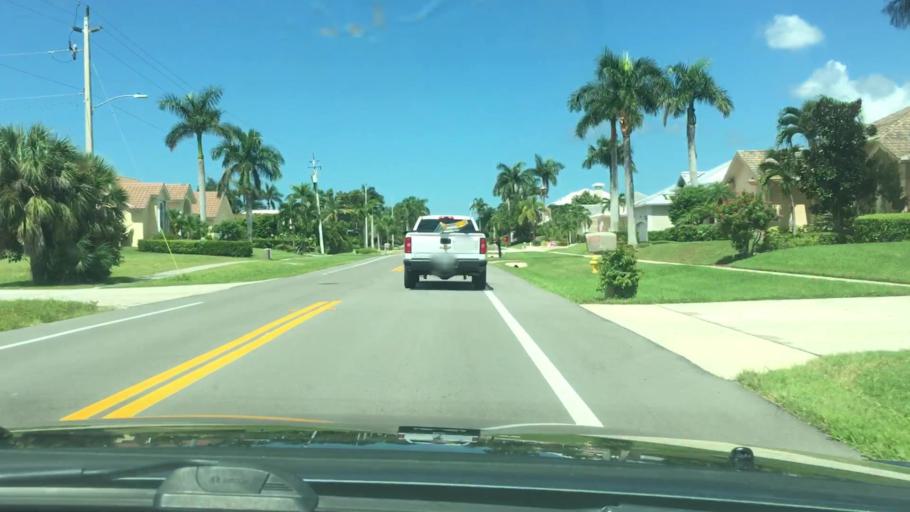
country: US
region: Florida
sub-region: Collier County
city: Marco
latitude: 25.9487
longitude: -81.7354
